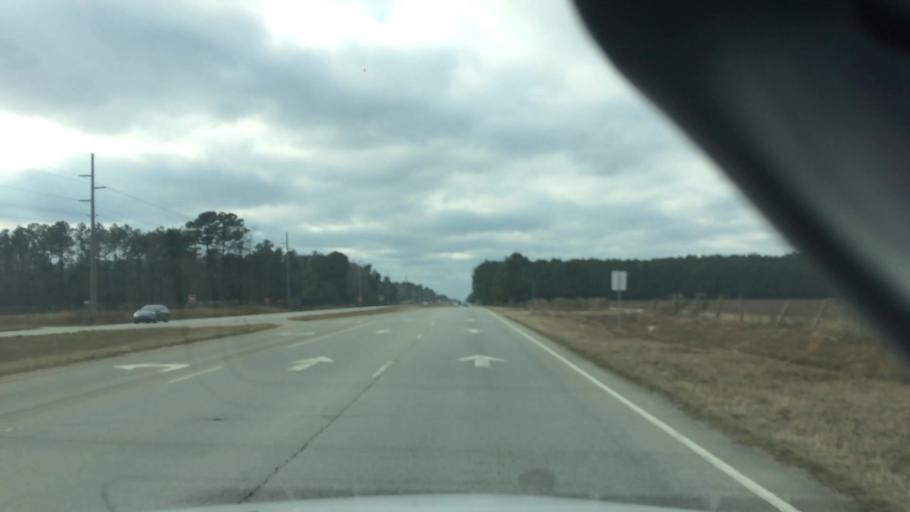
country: US
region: North Carolina
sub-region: Brunswick County
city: Shallotte
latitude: 33.9561
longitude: -78.4397
